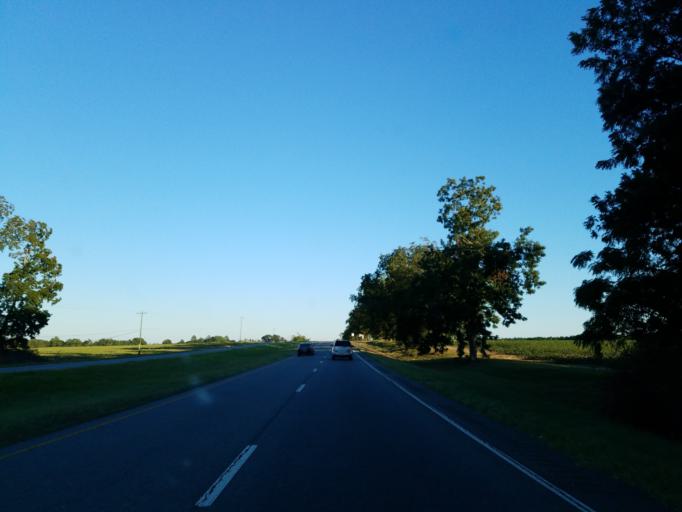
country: US
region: Georgia
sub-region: Worth County
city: Sylvester
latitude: 31.4999
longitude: -83.7150
